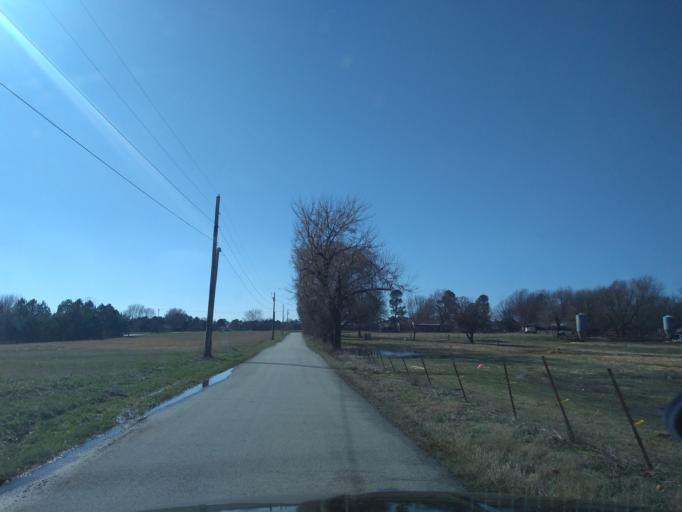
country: US
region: Arkansas
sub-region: Washington County
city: Farmington
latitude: 36.0675
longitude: -94.2505
